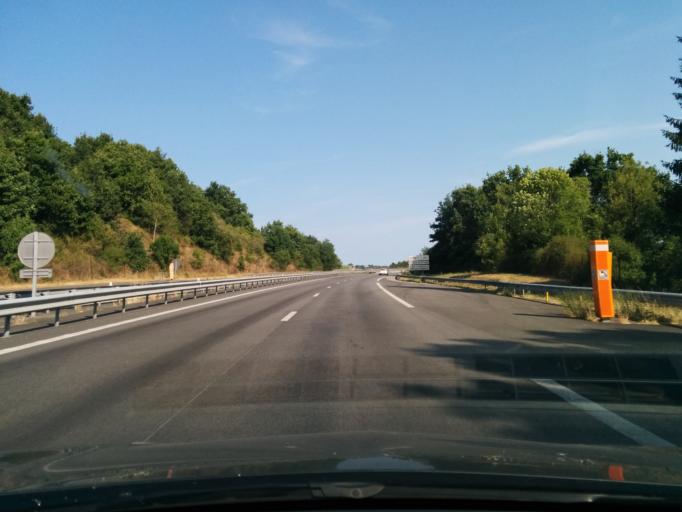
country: FR
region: Limousin
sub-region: Departement de la Haute-Vienne
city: Pierre-Buffiere
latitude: 45.6980
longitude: 1.3616
